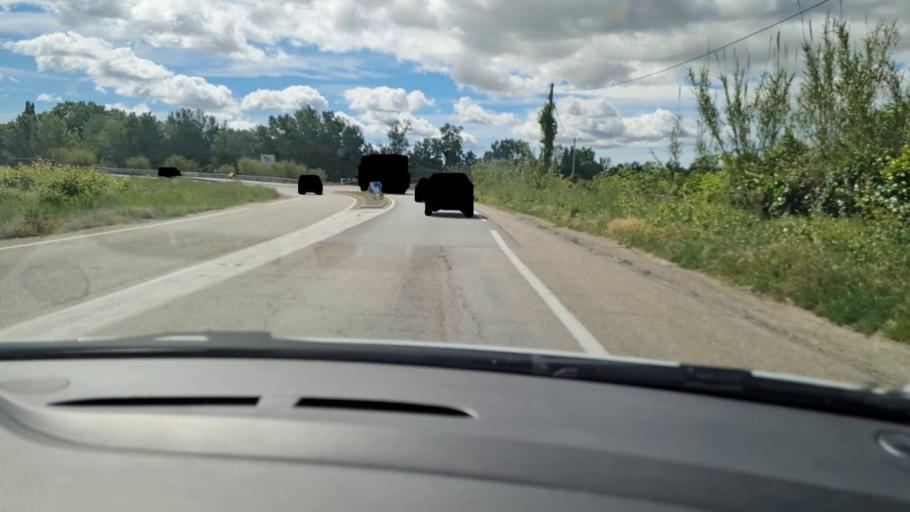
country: FR
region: Languedoc-Roussillon
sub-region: Departement du Gard
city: Caissargues
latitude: 43.7931
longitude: 4.3469
